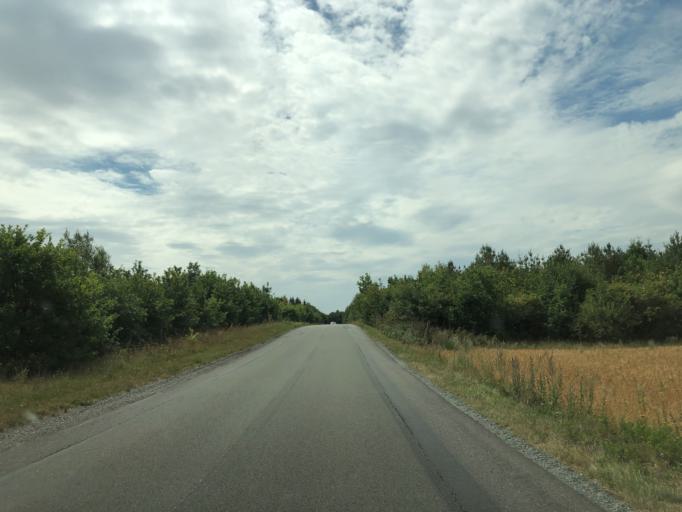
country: DK
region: South Denmark
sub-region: Vejle Kommune
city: Egtved
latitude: 55.6303
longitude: 9.1952
